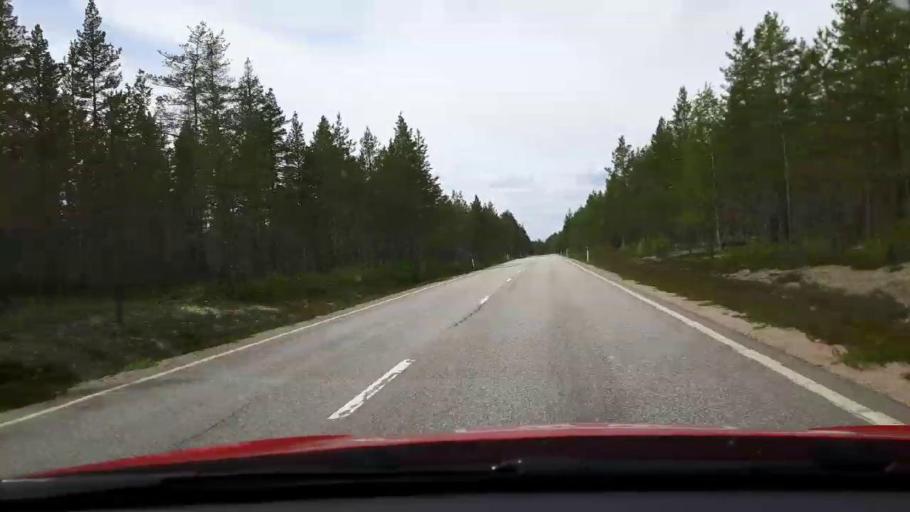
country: SE
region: Jaemtland
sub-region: Harjedalens Kommun
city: Sveg
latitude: 62.1252
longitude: 14.1047
